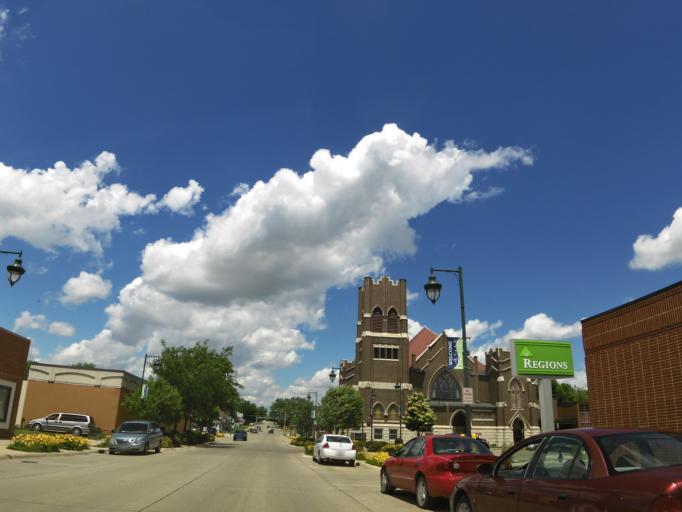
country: US
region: Iowa
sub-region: Fayette County
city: Oelwein
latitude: 42.6793
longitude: -91.9134
